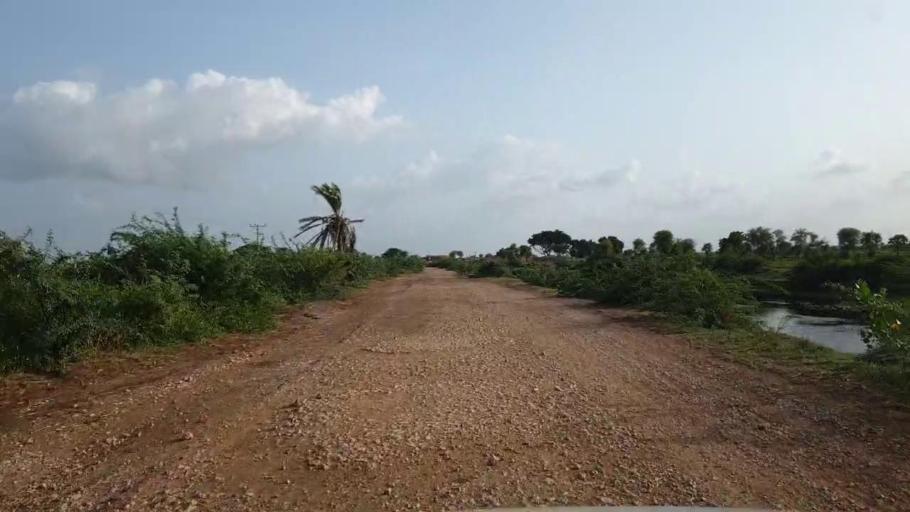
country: PK
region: Sindh
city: Kario
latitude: 24.8228
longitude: 68.6472
